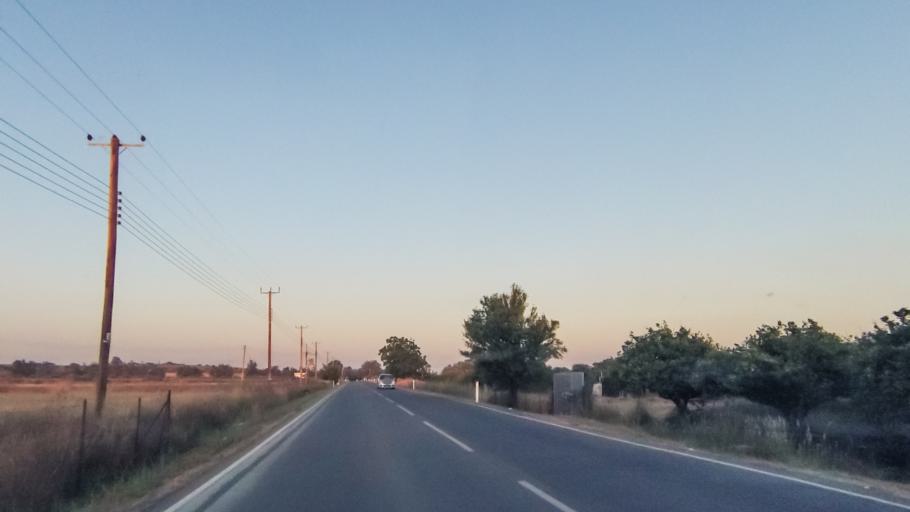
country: CY
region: Larnaka
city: Kolossi
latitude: 34.6570
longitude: 32.9184
